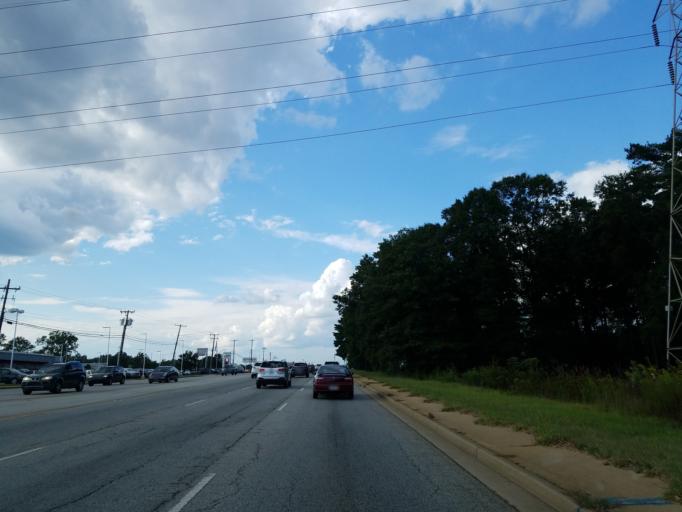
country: US
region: South Carolina
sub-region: Greenville County
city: Mauldin
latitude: 34.8172
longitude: -82.3395
